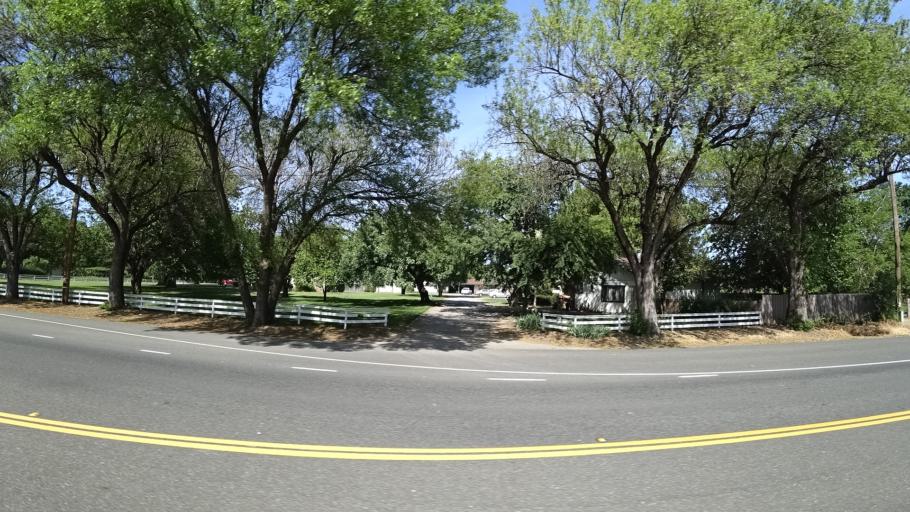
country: US
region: California
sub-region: Tehama County
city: Gerber
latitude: 40.1445
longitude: -122.1350
